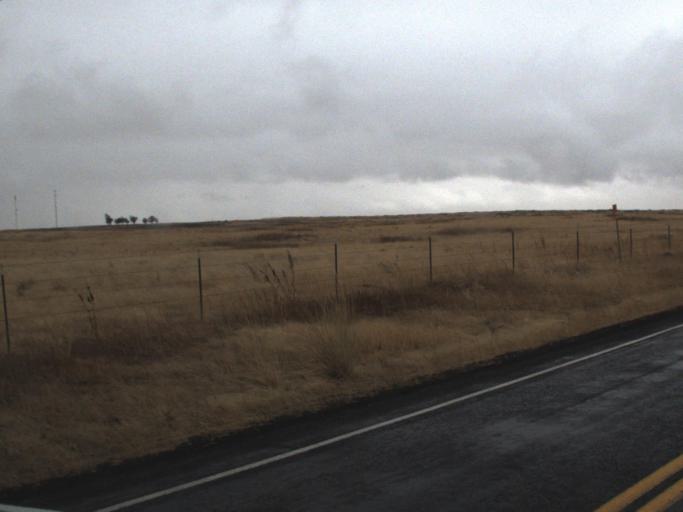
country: US
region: Washington
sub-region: Lincoln County
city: Davenport
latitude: 47.3236
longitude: -117.9814
